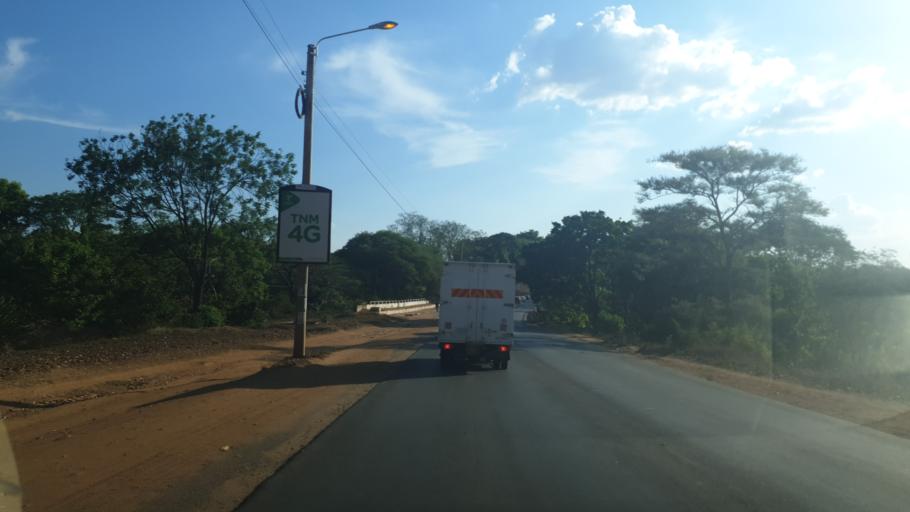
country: MW
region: Central Region
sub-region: Lilongwe District
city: Lilongwe
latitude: -13.9702
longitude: 33.7842
